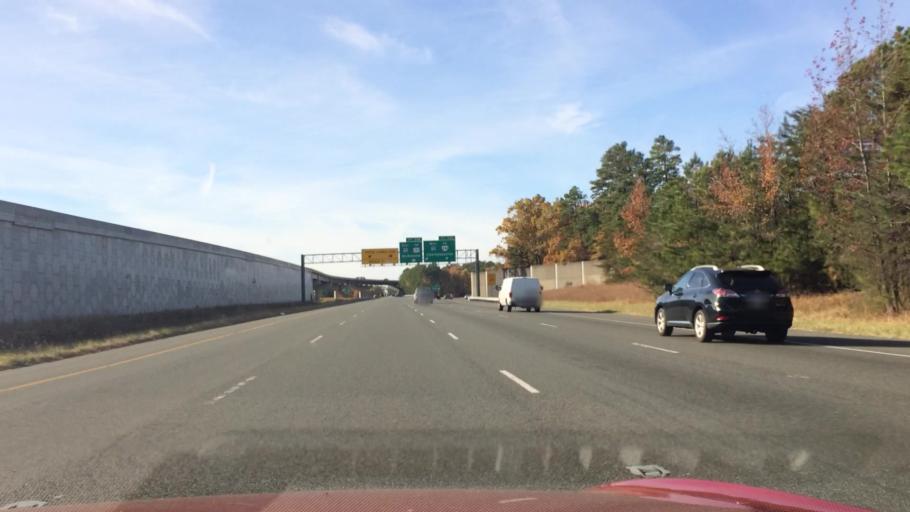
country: US
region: Virginia
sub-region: Henrico County
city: Short Pump
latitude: 37.6601
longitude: -77.6011
